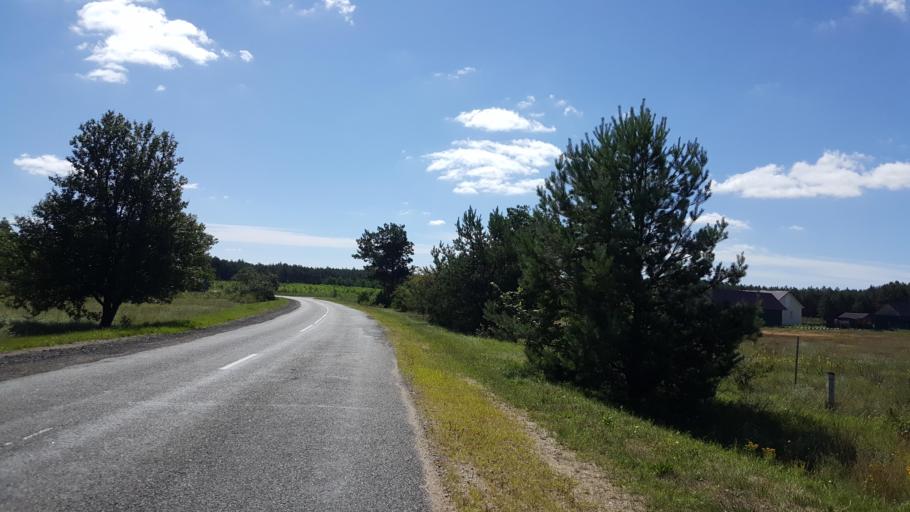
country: BY
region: Brest
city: Zhabinka
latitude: 52.3916
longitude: 24.0970
